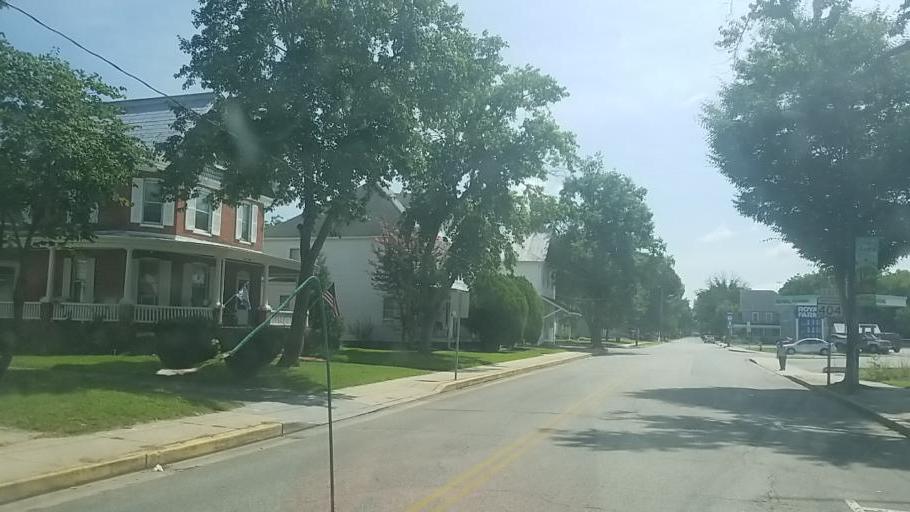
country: US
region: Maryland
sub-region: Caroline County
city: Denton
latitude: 38.8856
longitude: -75.8301
